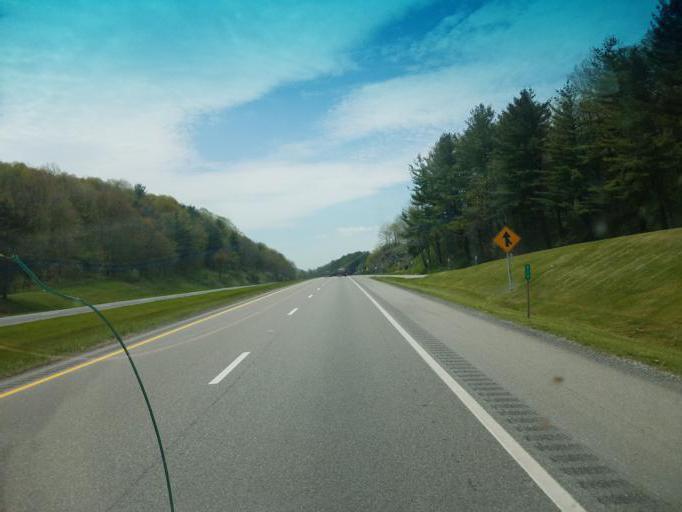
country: US
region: Virginia
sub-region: Smyth County
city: Atkins
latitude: 36.8829
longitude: -81.3860
